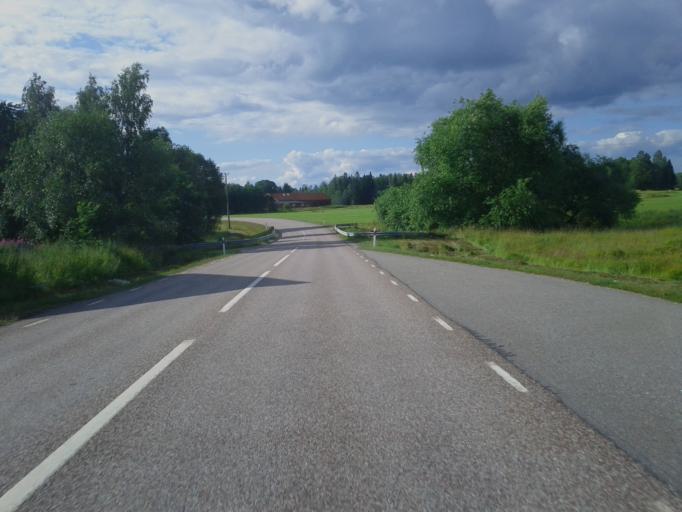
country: SE
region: Vaestmanland
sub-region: Sala Kommun
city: Sala
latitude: 59.9137
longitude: 16.5189
